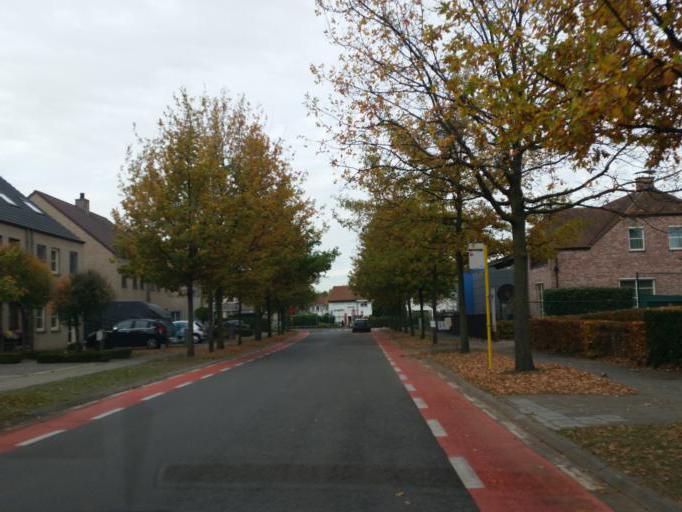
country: BE
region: Flanders
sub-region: Provincie Vlaams-Brabant
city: Machelen
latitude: 50.9173
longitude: 4.4473
